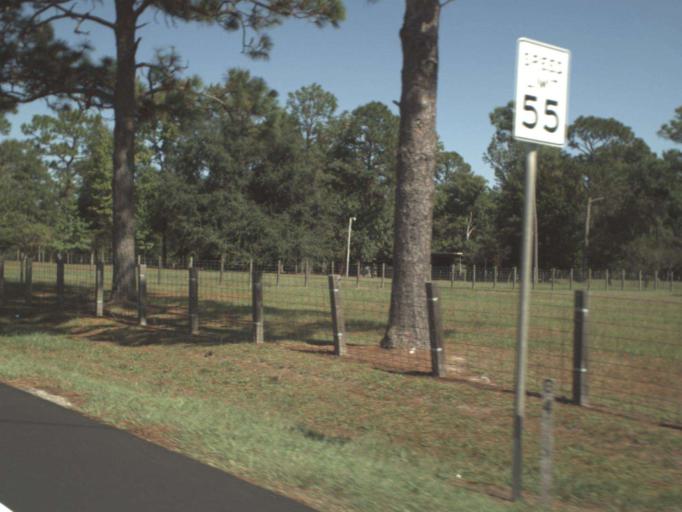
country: US
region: Florida
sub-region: Walton County
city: DeFuniak Springs
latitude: 30.7488
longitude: -86.1479
